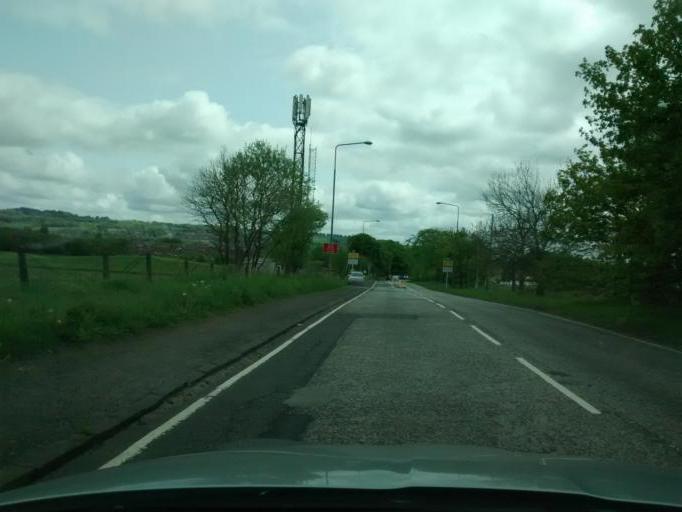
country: GB
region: Scotland
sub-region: West Lothian
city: Bathgate
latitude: 55.9003
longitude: -3.6692
